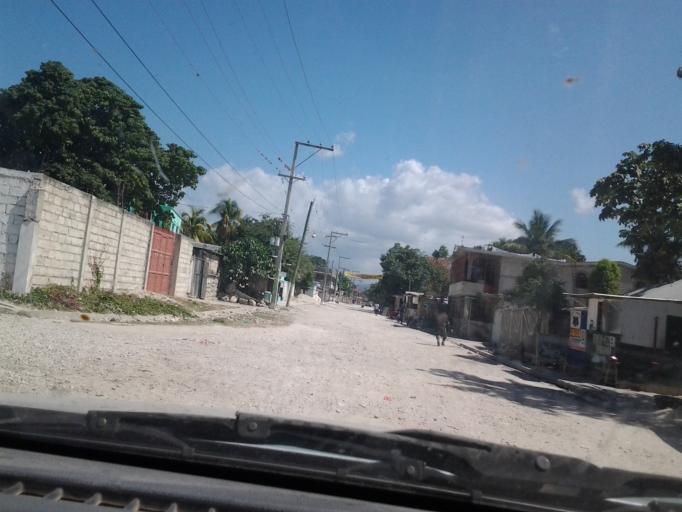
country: HT
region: Ouest
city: Grangwav
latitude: 18.4271
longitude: -72.7718
